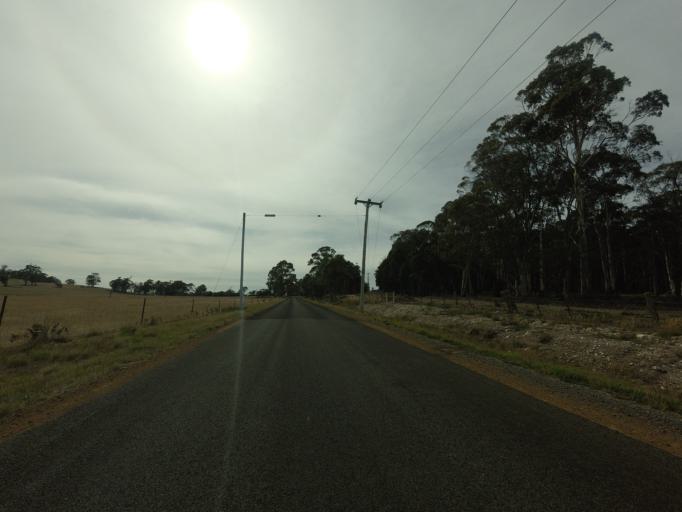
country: AU
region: Tasmania
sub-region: Sorell
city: Sorell
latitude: -42.4261
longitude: 147.4843
